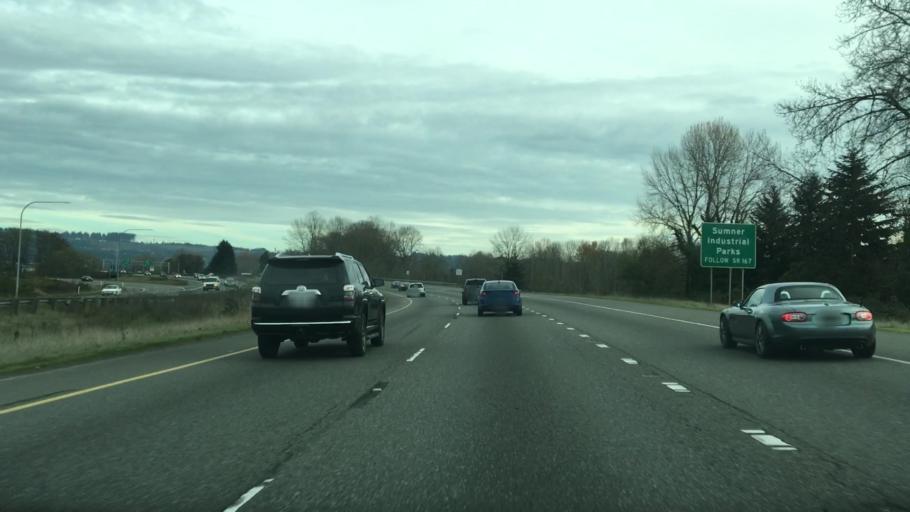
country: US
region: Washington
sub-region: Pierce County
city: North Puyallup
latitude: 47.2006
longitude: -122.2664
